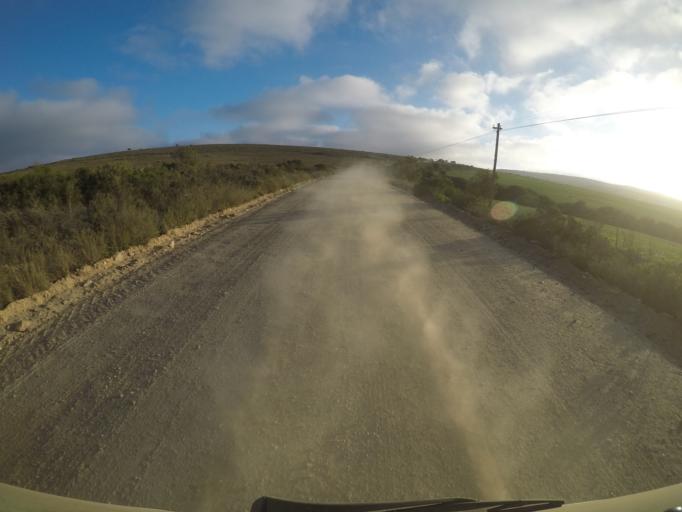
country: ZA
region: Western Cape
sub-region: Eden District Municipality
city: Mossel Bay
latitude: -34.1256
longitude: 22.0518
